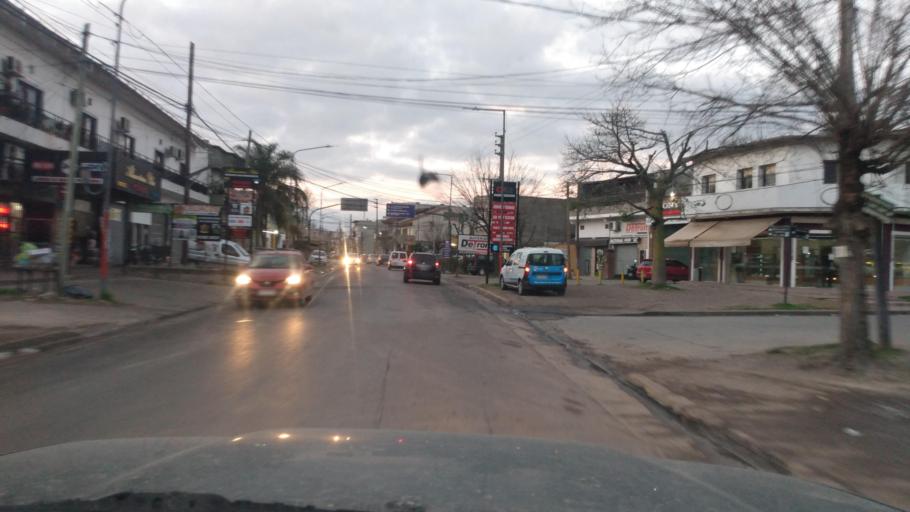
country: AR
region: Buenos Aires
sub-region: Partido de Pilar
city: Pilar
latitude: -34.4661
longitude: -58.9150
